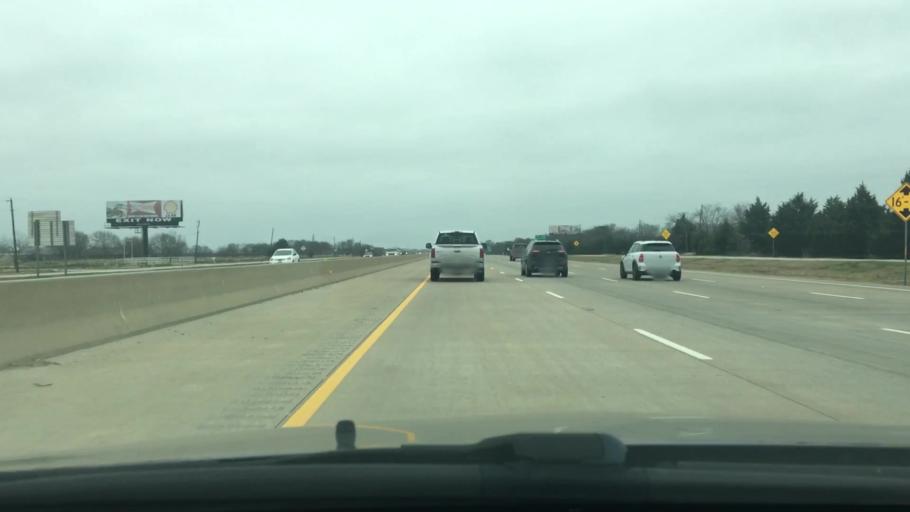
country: US
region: Texas
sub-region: Ellis County
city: Ennis
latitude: 32.2543
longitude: -96.5021
